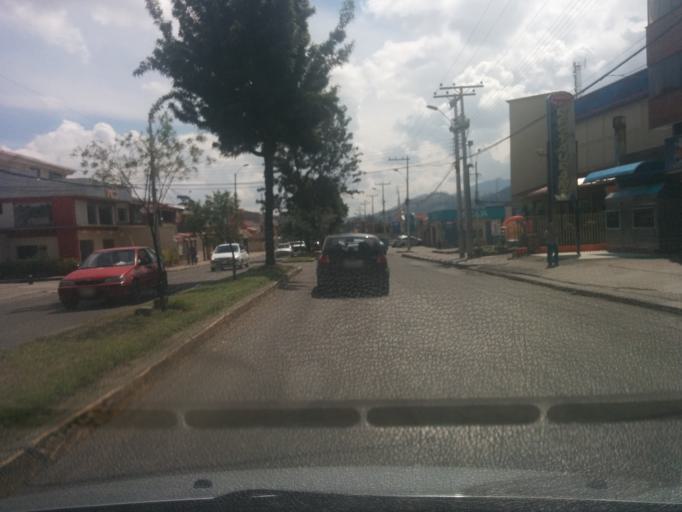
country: EC
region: Azuay
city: Cuenca
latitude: -2.8993
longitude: -78.9848
